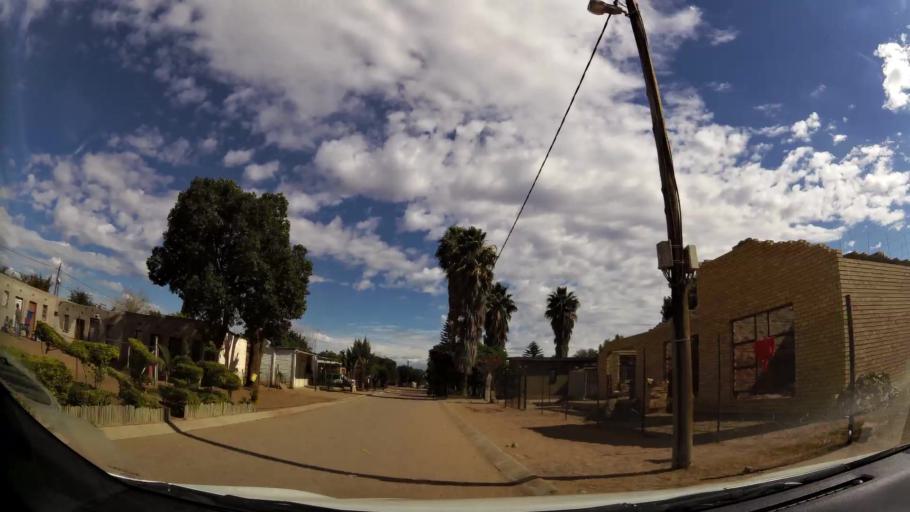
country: ZA
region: Limpopo
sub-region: Waterberg District Municipality
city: Bela-Bela
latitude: -24.8914
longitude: 28.3209
